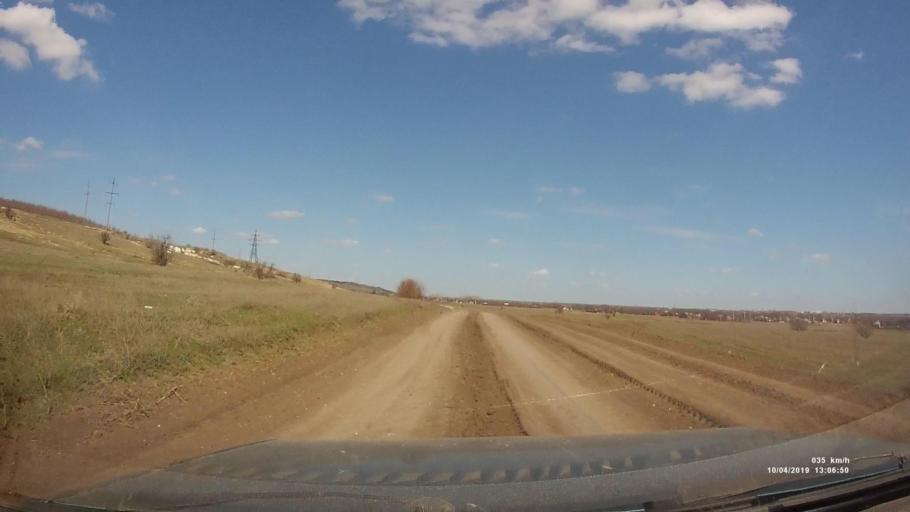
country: RU
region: Rostov
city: Masalovka
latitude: 48.3930
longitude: 40.2378
